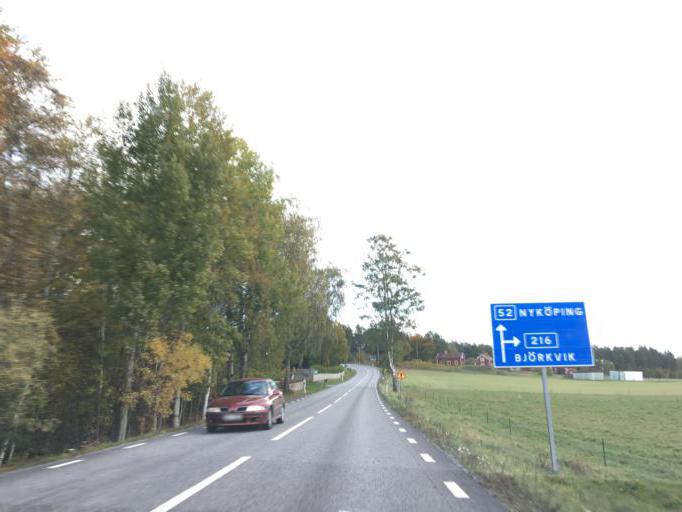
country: SE
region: Soedermanland
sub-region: Flens Kommun
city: Flen
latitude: 58.9122
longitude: 16.4398
